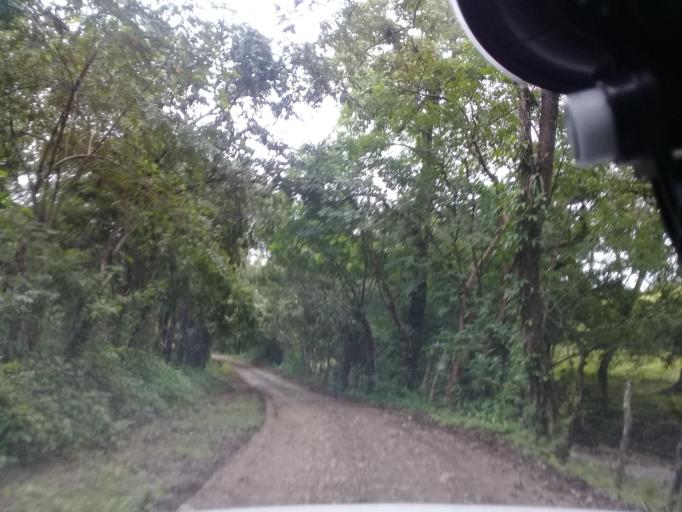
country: MX
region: Veracruz
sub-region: Chalma
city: San Pedro Coyutla
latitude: 21.2376
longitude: -98.4313
